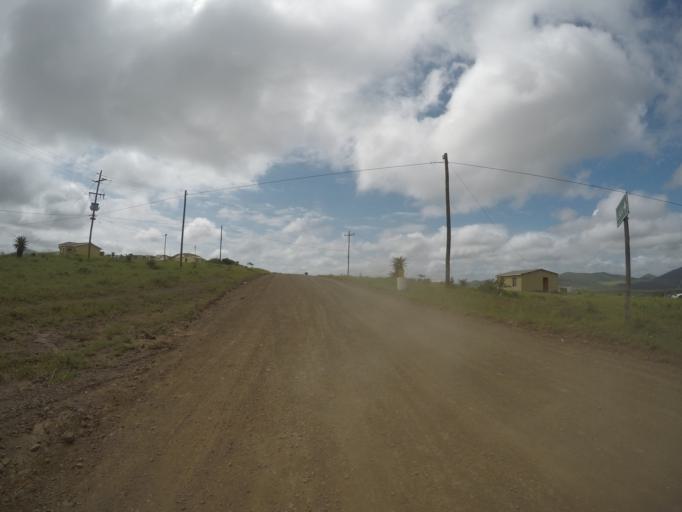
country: ZA
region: KwaZulu-Natal
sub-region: uThungulu District Municipality
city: Empangeni
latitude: -28.6030
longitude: 31.8418
